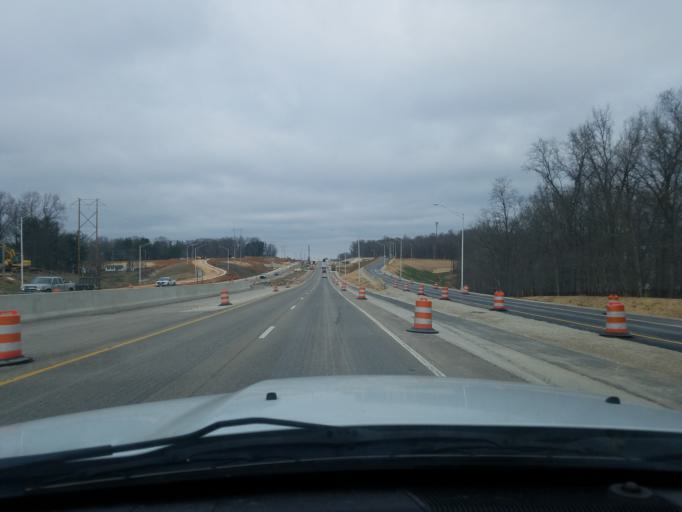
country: US
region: Indiana
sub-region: Monroe County
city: Bloomington
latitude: 39.1327
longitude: -86.5729
